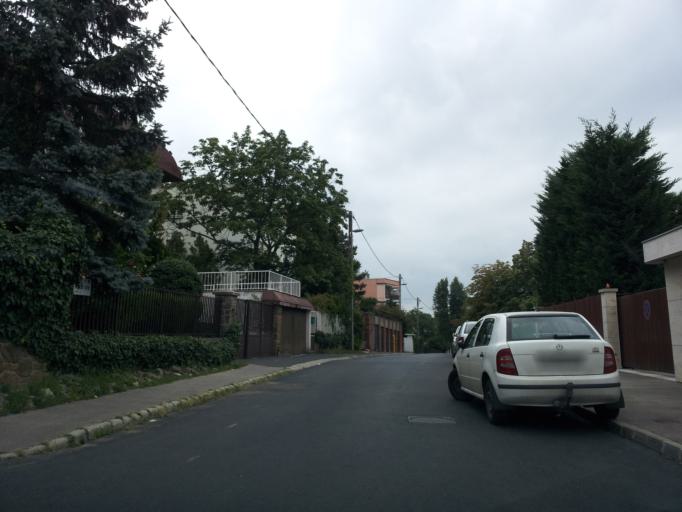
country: HU
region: Budapest
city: Budapest II. keruelet
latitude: 47.5201
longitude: 19.0126
